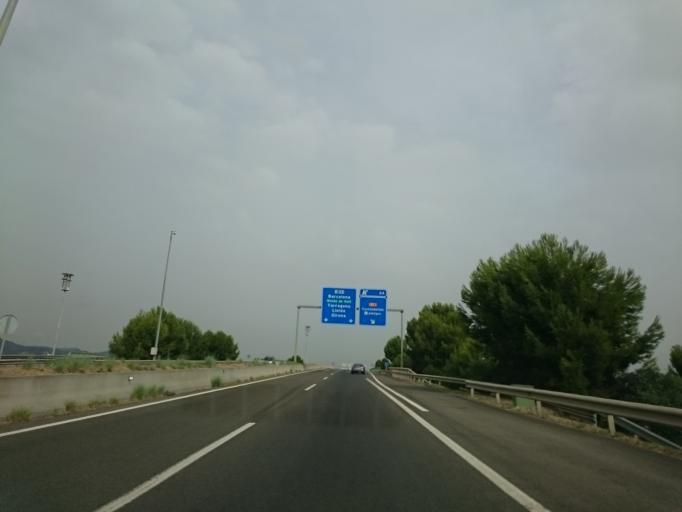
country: ES
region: Catalonia
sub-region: Provincia de Barcelona
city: El Prat de Llobregat
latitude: 41.3202
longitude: 2.0757
